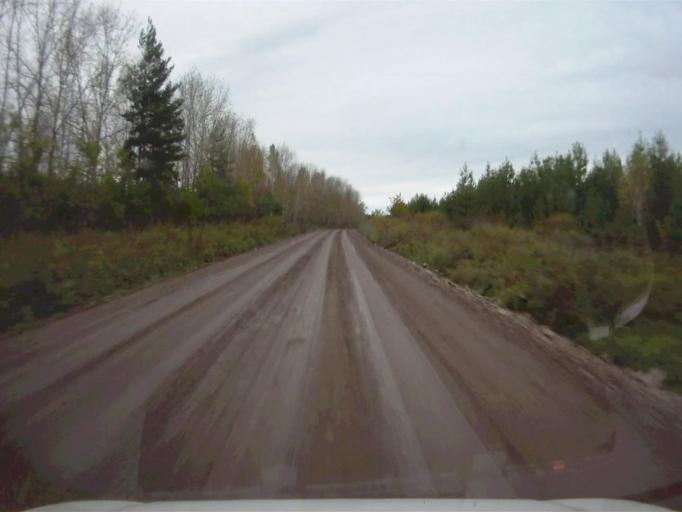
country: RU
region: Chelyabinsk
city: Nyazepetrovsk
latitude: 56.1360
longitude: 59.3024
